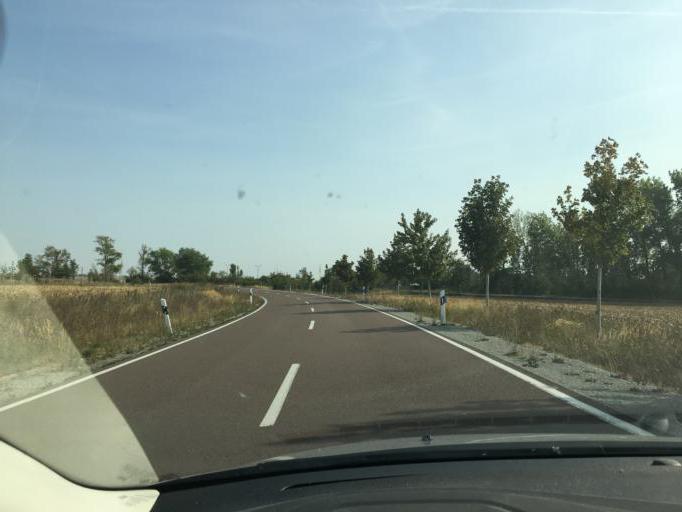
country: DE
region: Saxony-Anhalt
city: Baalberge
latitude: 51.8100
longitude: 11.8127
